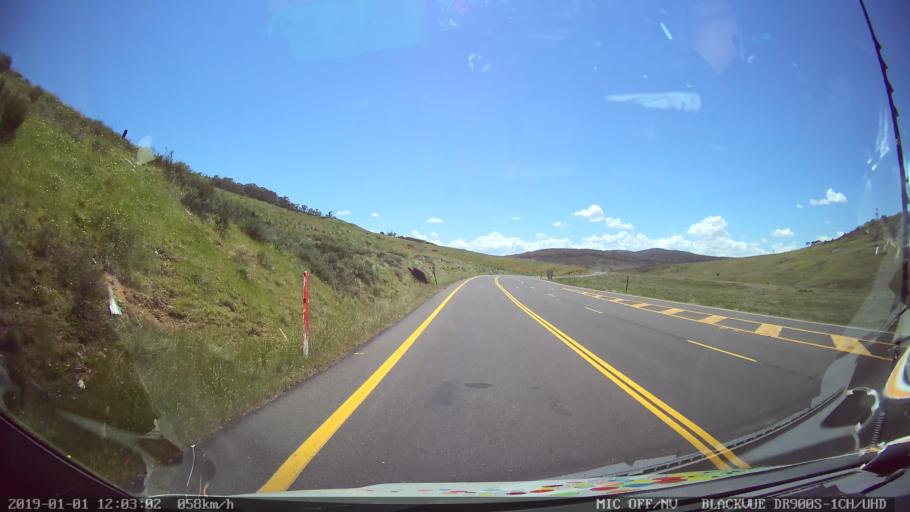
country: AU
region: New South Wales
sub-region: Snowy River
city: Jindabyne
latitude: -35.8701
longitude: 148.4826
